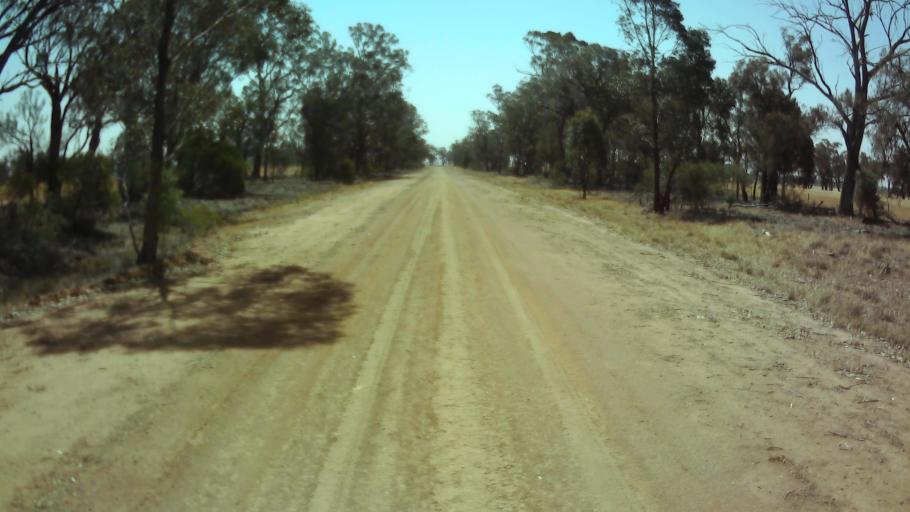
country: AU
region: New South Wales
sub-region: Weddin
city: Grenfell
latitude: -33.9406
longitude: 147.8111
